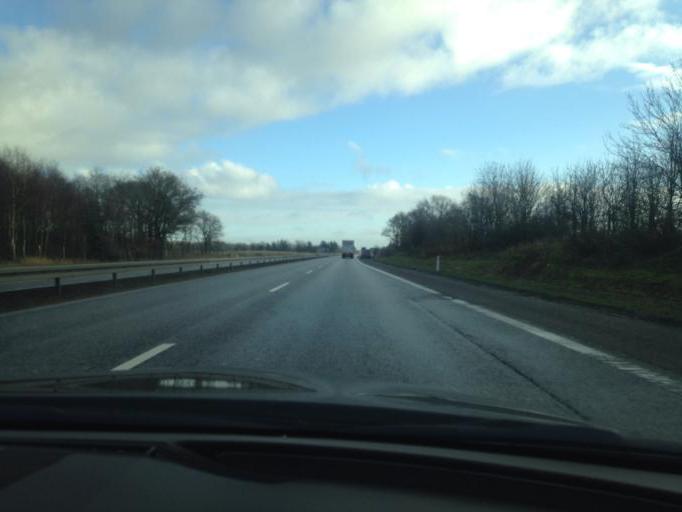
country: DK
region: South Denmark
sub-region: Vejen Kommune
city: Vejen
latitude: 55.4938
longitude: 9.1395
